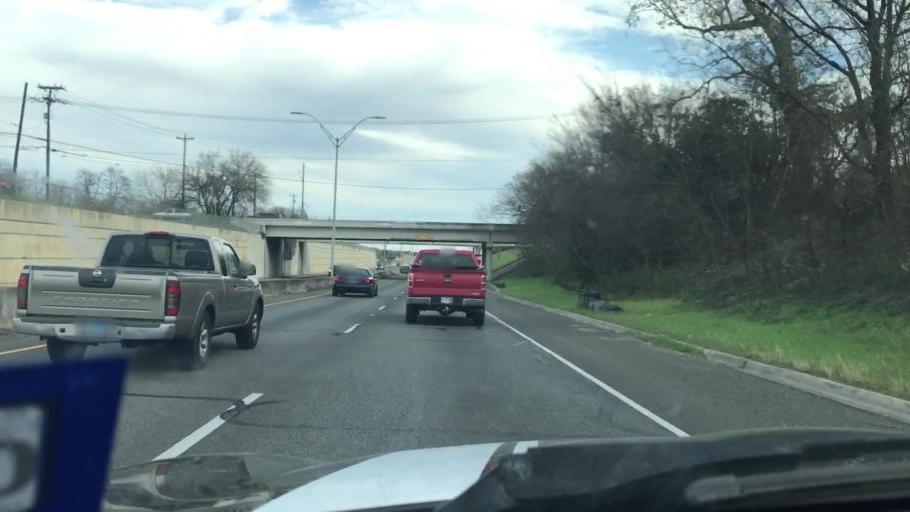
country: US
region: Texas
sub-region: Bastrop County
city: Elgin
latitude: 30.3366
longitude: -97.3680
